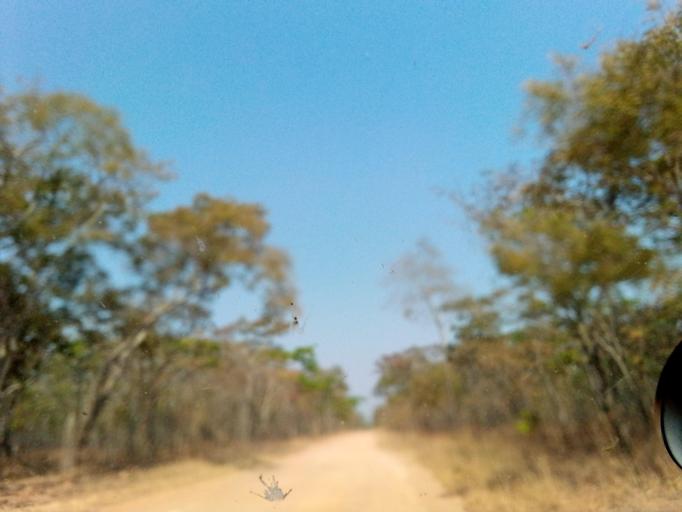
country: ZM
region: Northern
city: Mpika
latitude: -12.2420
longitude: 30.8475
